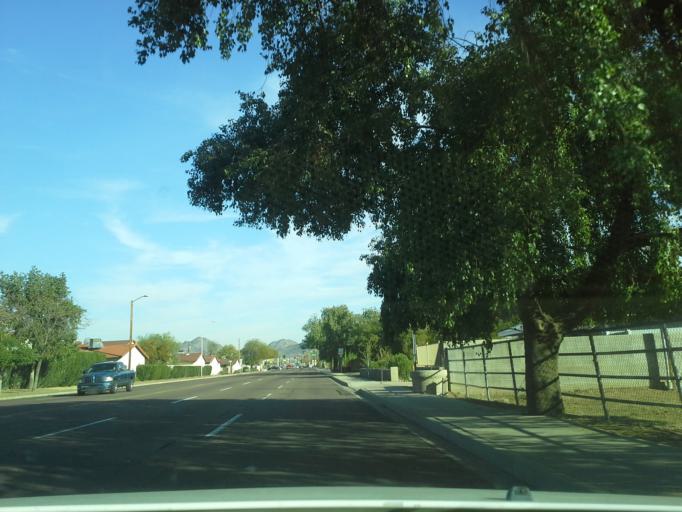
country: US
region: Arizona
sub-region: Maricopa County
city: Glendale
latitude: 33.5675
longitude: -112.0861
